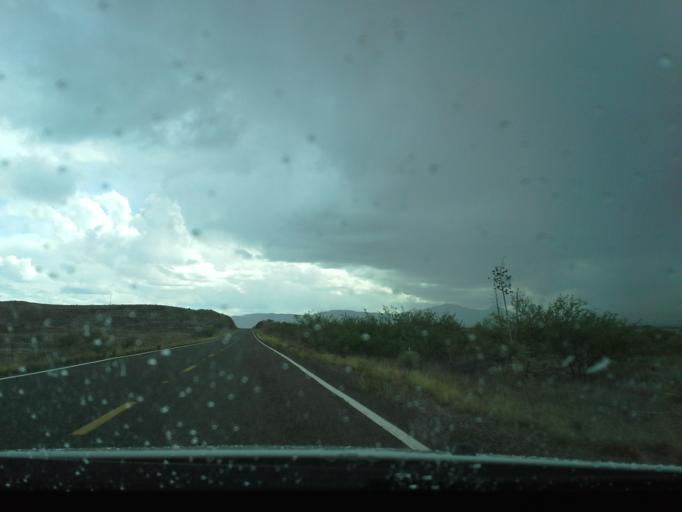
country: US
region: Arizona
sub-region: Cochise County
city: Douglas
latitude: 31.5399
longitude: -109.2876
